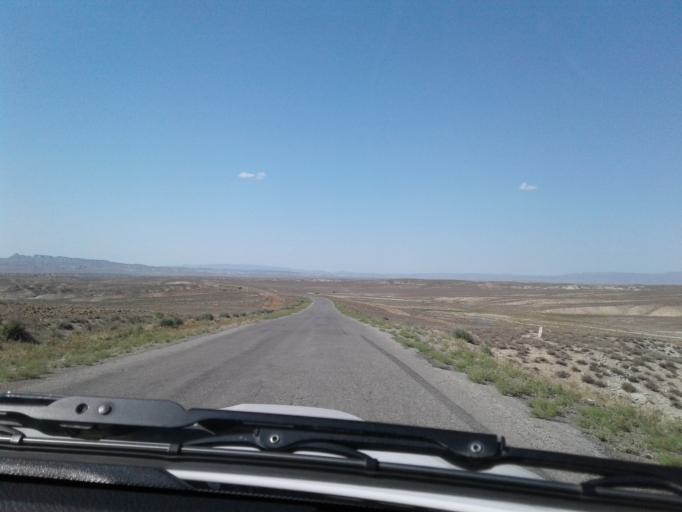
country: TM
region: Balkan
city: Magtymguly
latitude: 38.5410
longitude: 56.1920
